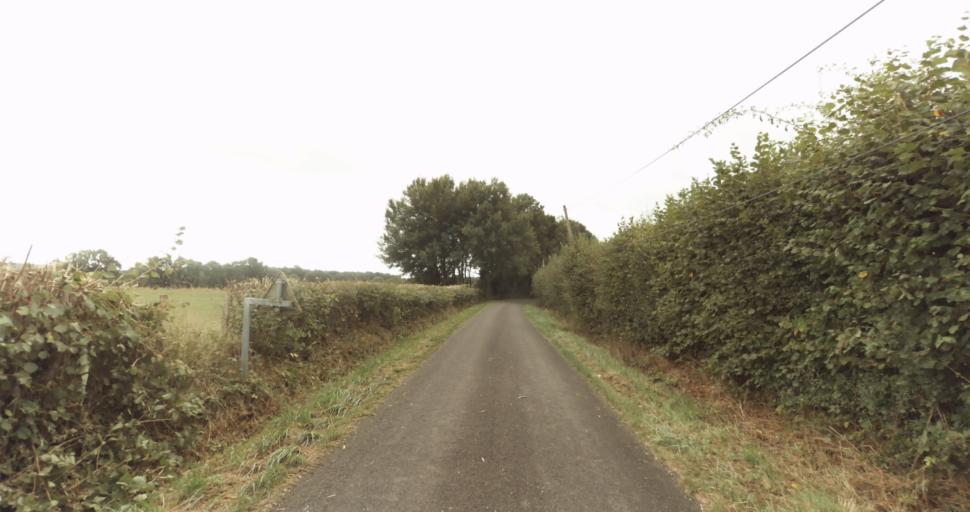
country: FR
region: Lower Normandy
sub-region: Departement de l'Orne
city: Sainte-Gauburge-Sainte-Colombe
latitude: 48.7152
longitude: 0.4882
